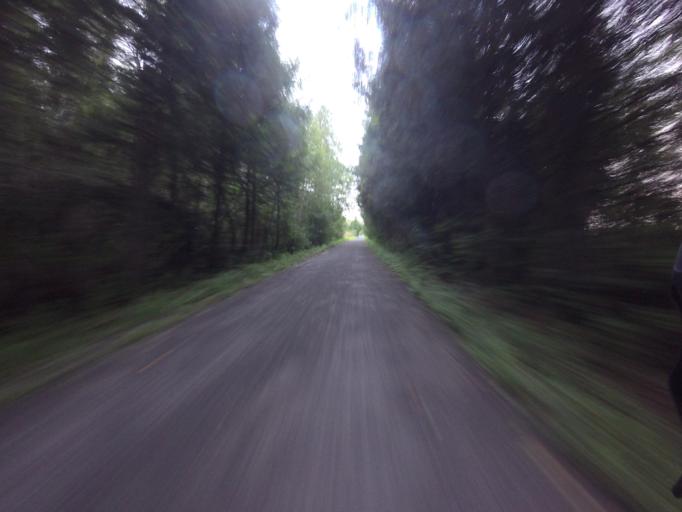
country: CA
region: Ontario
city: Carleton Place
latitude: 45.1900
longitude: -76.0287
